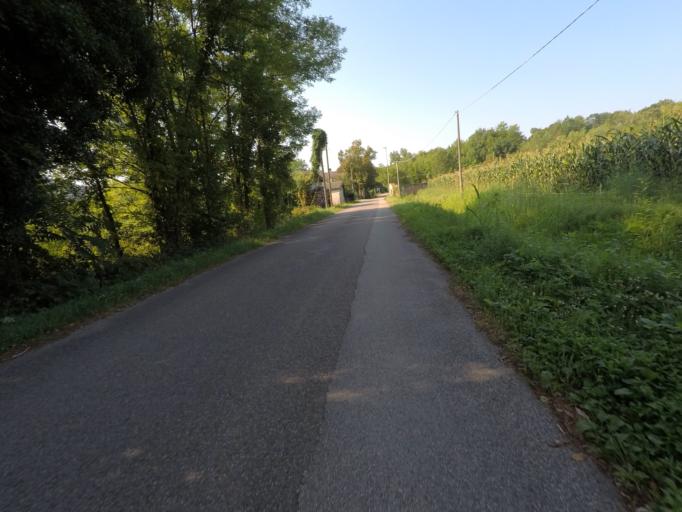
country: IT
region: Friuli Venezia Giulia
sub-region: Provincia di Pordenone
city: Pinzano al Tagliamento
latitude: 46.1961
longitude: 12.9563
